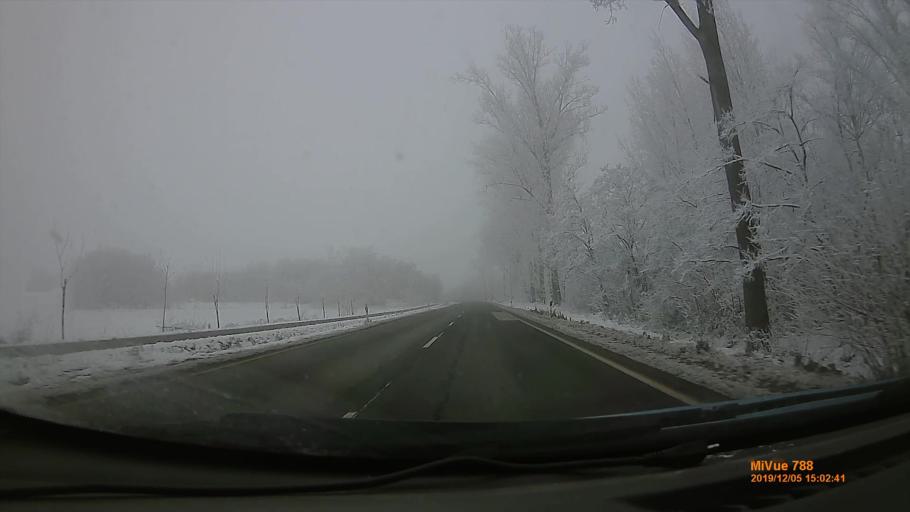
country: HU
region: Szabolcs-Szatmar-Bereg
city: Tiszanagyfalu
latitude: 48.0782
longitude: 21.5104
